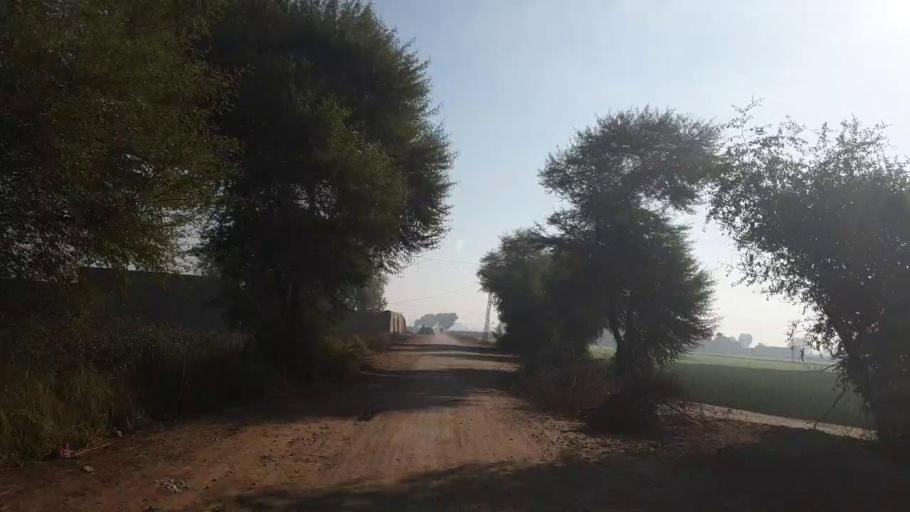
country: PK
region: Sindh
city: Dadu
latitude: 26.6764
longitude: 67.7790
